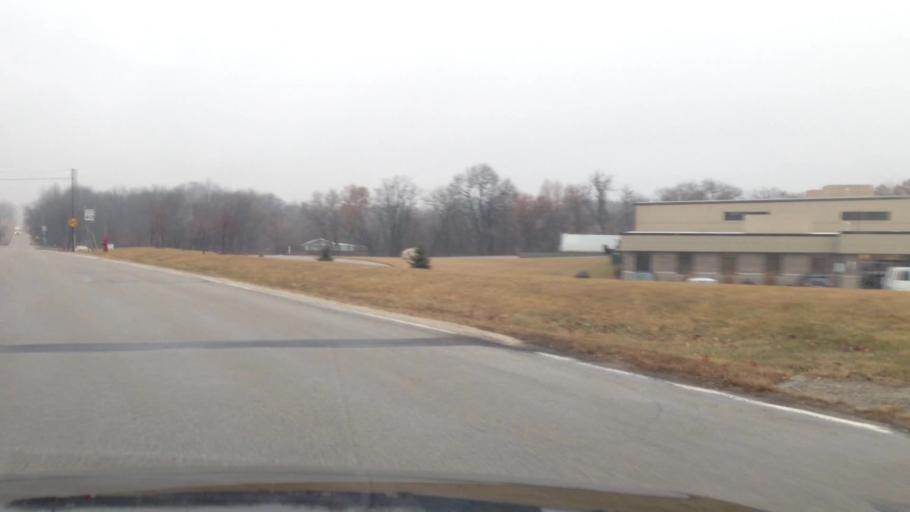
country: US
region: Wisconsin
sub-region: Washington County
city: Germantown
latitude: 43.2357
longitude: -88.1429
